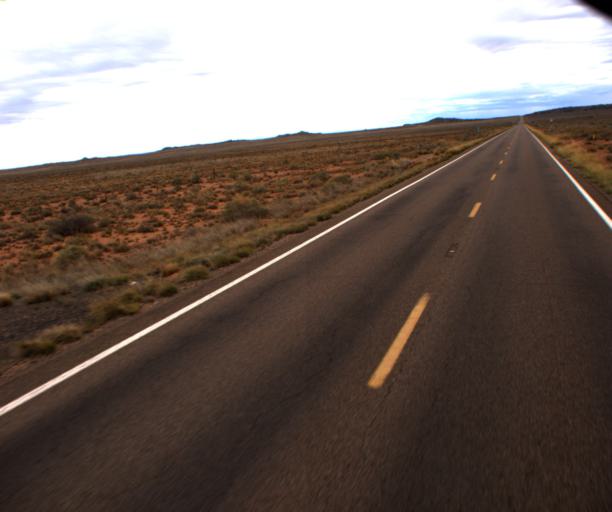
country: US
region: Arizona
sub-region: Navajo County
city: Holbrook
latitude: 34.7275
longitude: -110.1159
